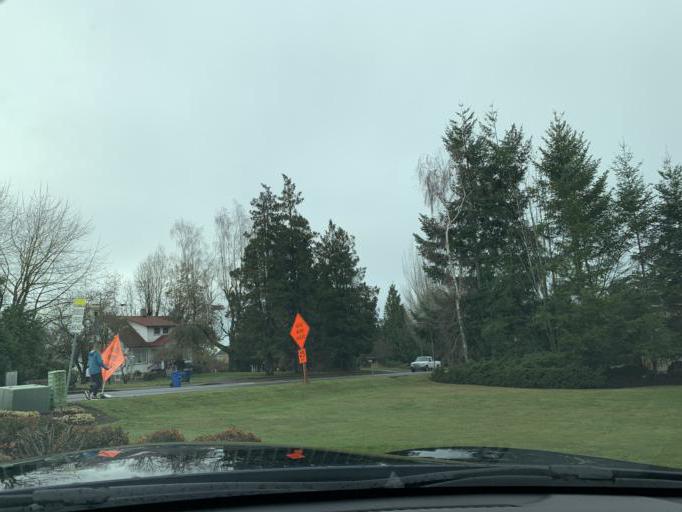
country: US
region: Washington
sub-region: Clark County
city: Camas
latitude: 45.5909
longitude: -122.4499
